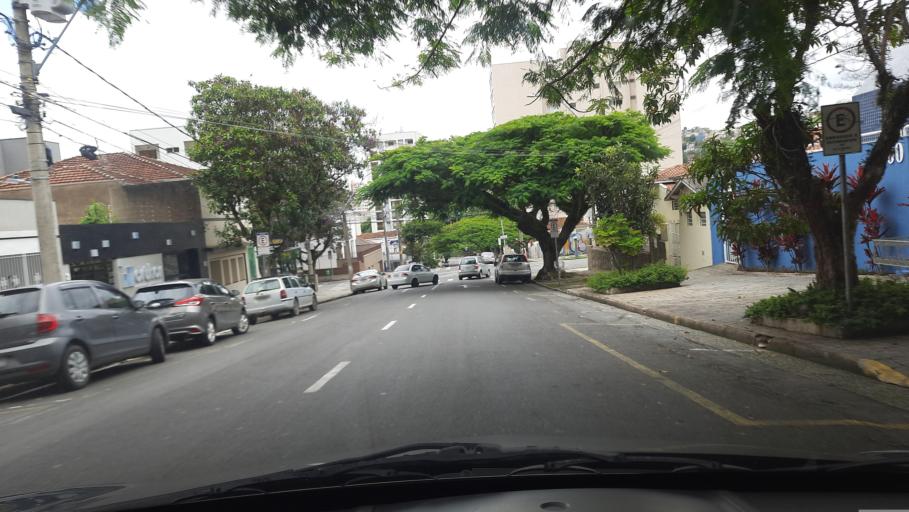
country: BR
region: Minas Gerais
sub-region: Pocos De Caldas
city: Pocos de Caldas
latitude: -21.7826
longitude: -46.5681
